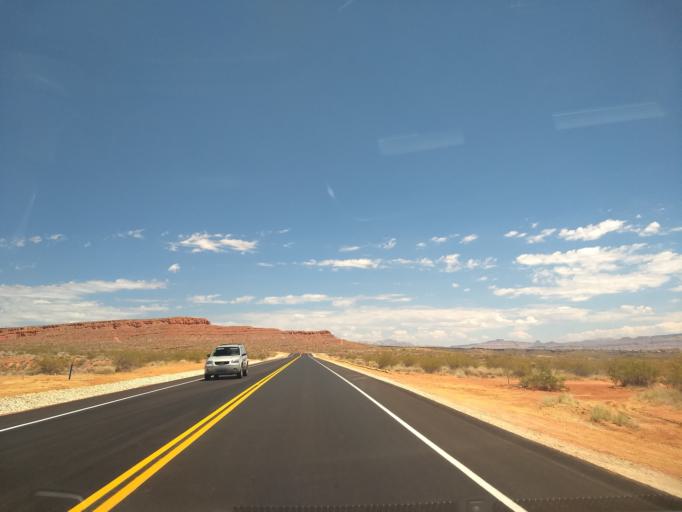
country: US
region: Utah
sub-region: Washington County
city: Washington
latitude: 37.1488
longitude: -113.5009
